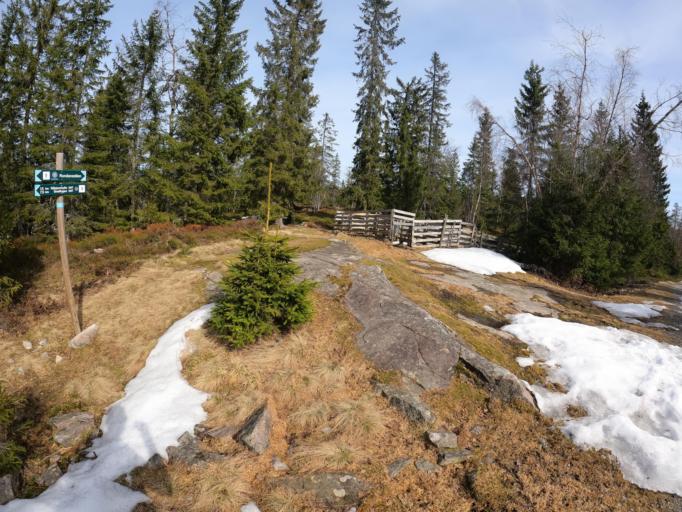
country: NO
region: Akershus
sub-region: Nannestad
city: Teigebyen
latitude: 60.2449
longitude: 10.8769
